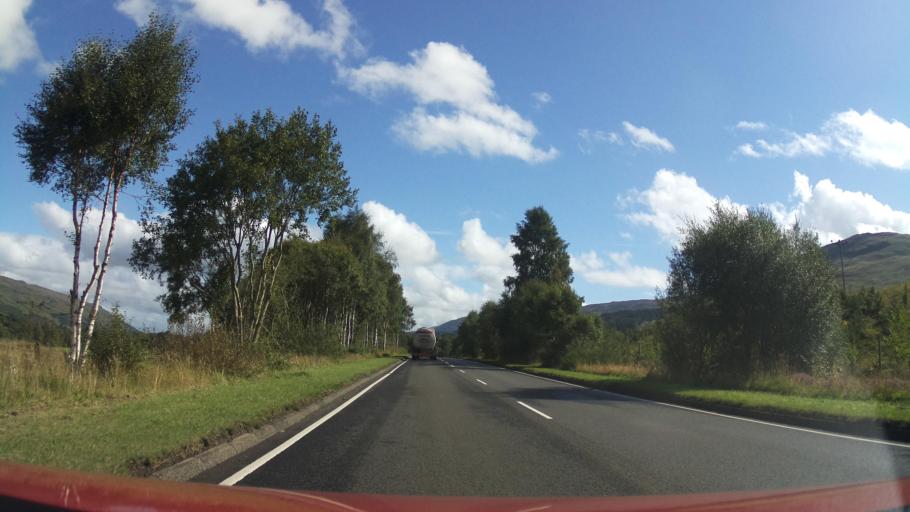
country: GB
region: Scotland
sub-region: Stirling
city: Callander
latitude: 56.4201
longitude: -4.4370
